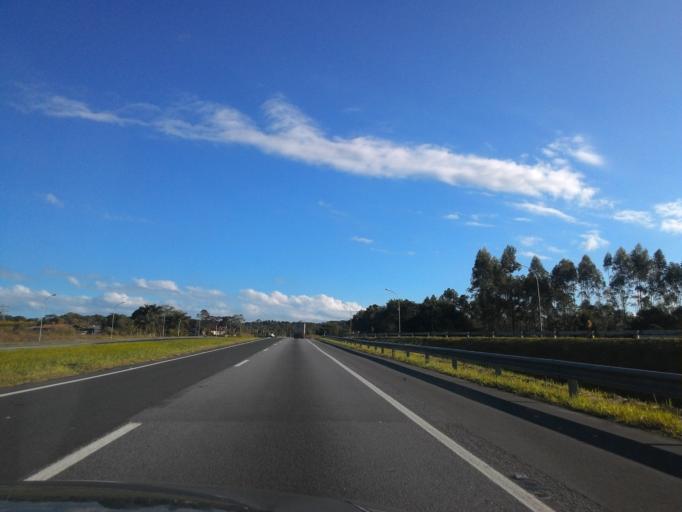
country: BR
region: Sao Paulo
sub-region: Pariquera-Acu
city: Pariquera Acu
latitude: -24.6453
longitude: -47.9198
